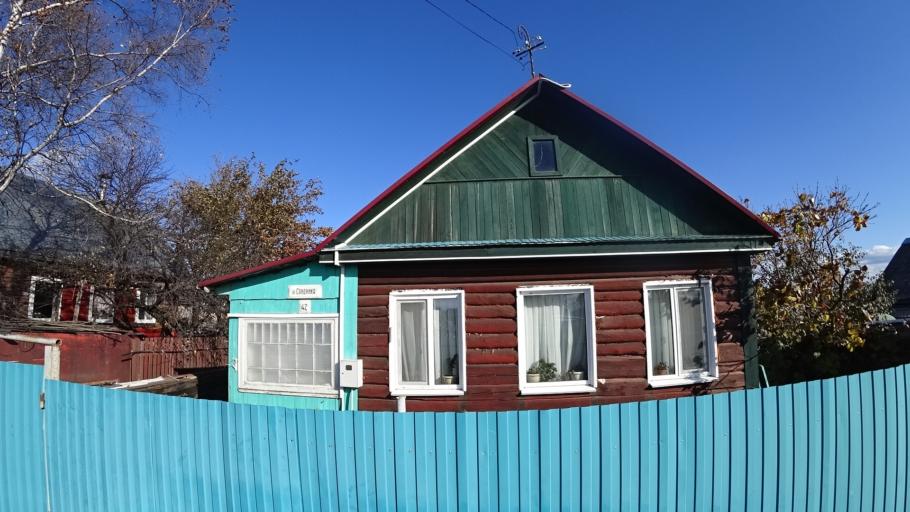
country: RU
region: Khabarovsk Krai
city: Amursk
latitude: 50.2337
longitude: 136.9213
